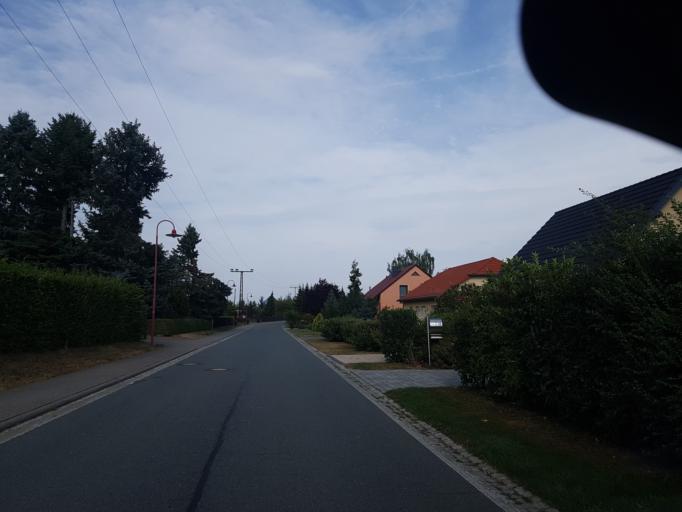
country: DE
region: Saxony
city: Stauchitz
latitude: 51.2649
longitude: 13.2344
